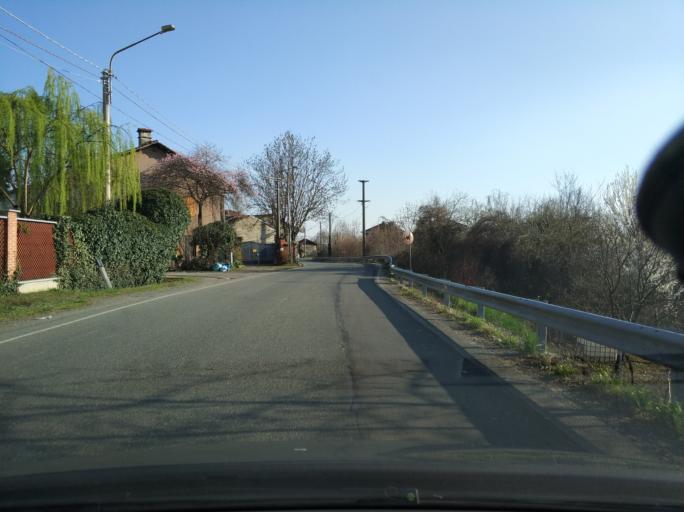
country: IT
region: Piedmont
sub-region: Provincia di Torino
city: Cirie
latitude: 45.2071
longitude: 7.5976
